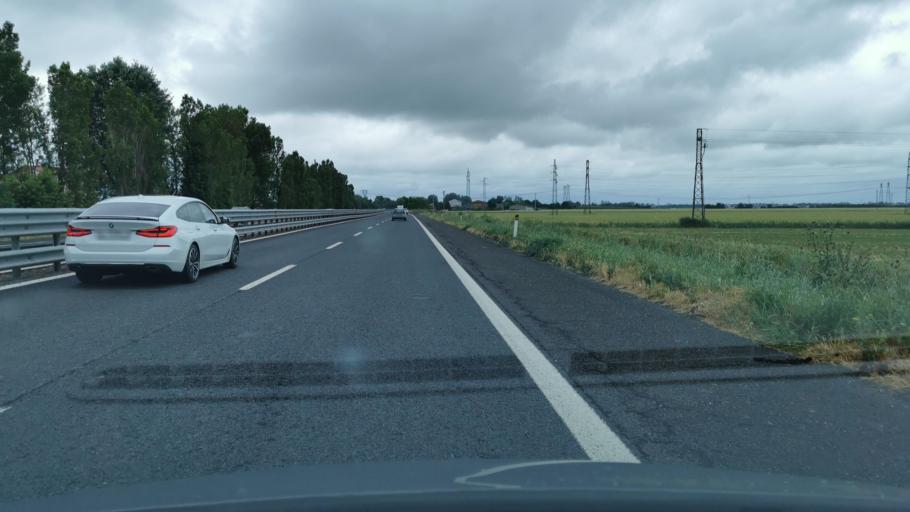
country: IT
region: Emilia-Romagna
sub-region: Provincia di Ravenna
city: Fornace Zarattini
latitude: 44.4208
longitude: 12.1418
